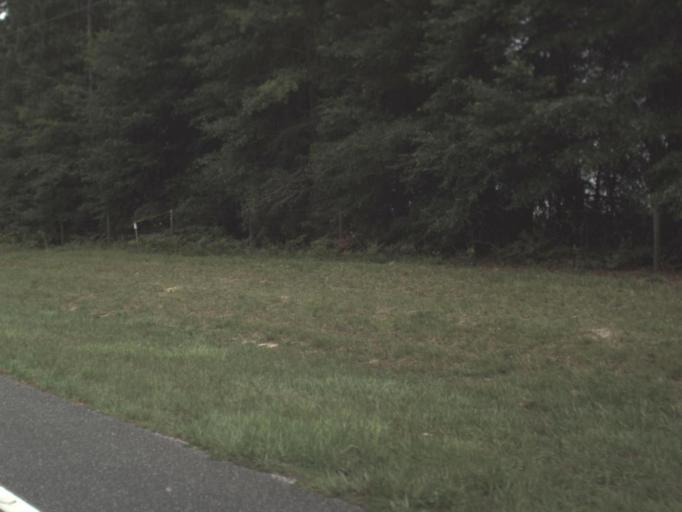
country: US
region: Florida
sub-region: Suwannee County
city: Wellborn
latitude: 30.0165
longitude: -82.8403
